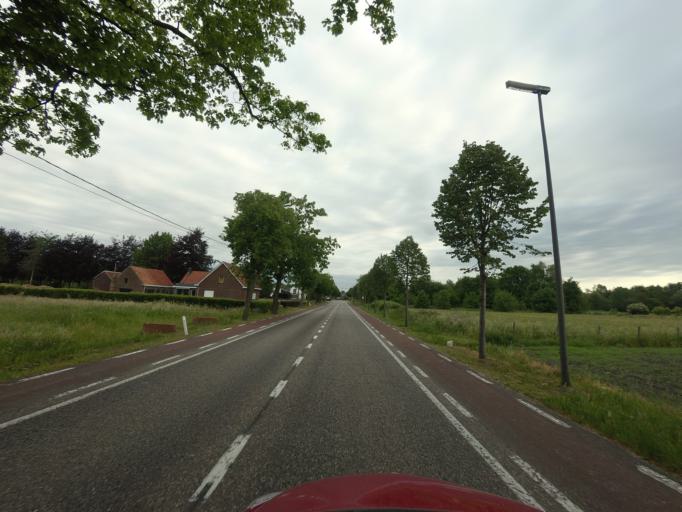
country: BE
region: Flanders
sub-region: Provincie Limburg
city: Leopoldsburg
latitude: 51.1567
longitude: 5.2614
